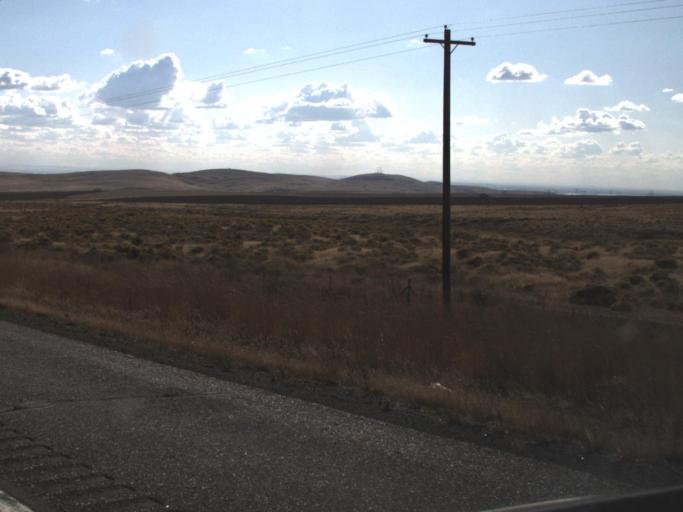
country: US
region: Washington
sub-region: Benton County
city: Highland
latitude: 46.0365
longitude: -119.2248
